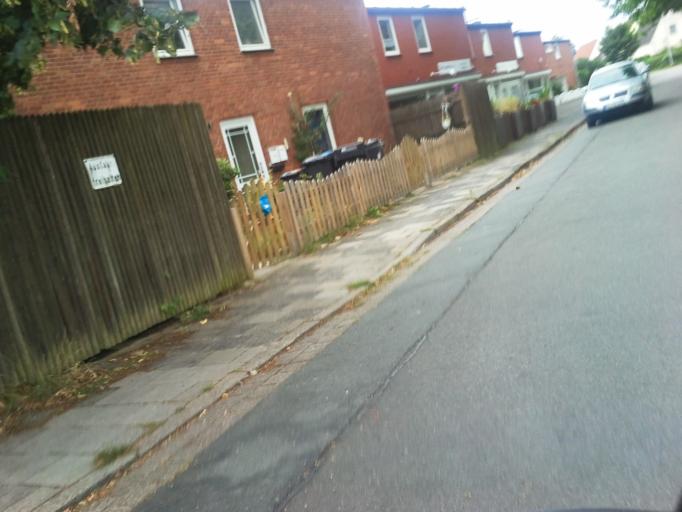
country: DE
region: Lower Saxony
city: Nienburg
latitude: 52.6556
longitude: 9.2188
